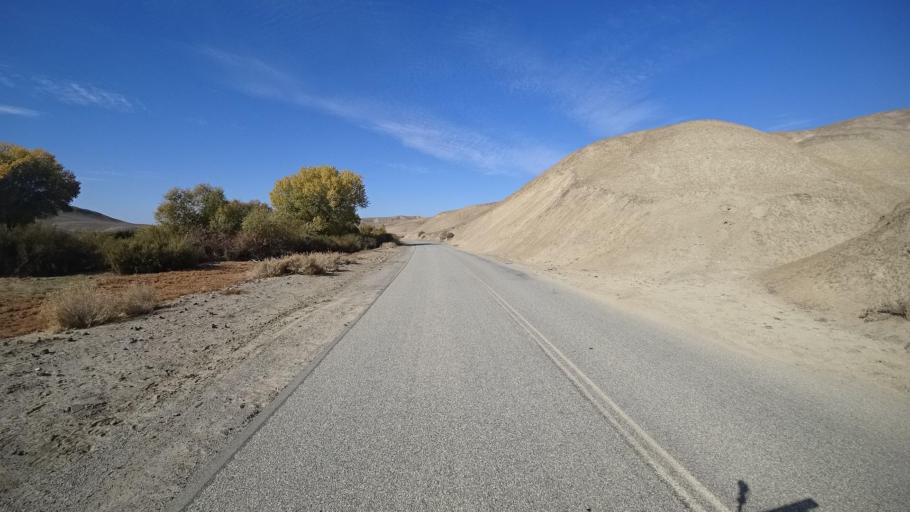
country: US
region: California
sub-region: Kern County
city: Oildale
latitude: 35.5212
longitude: -118.9295
